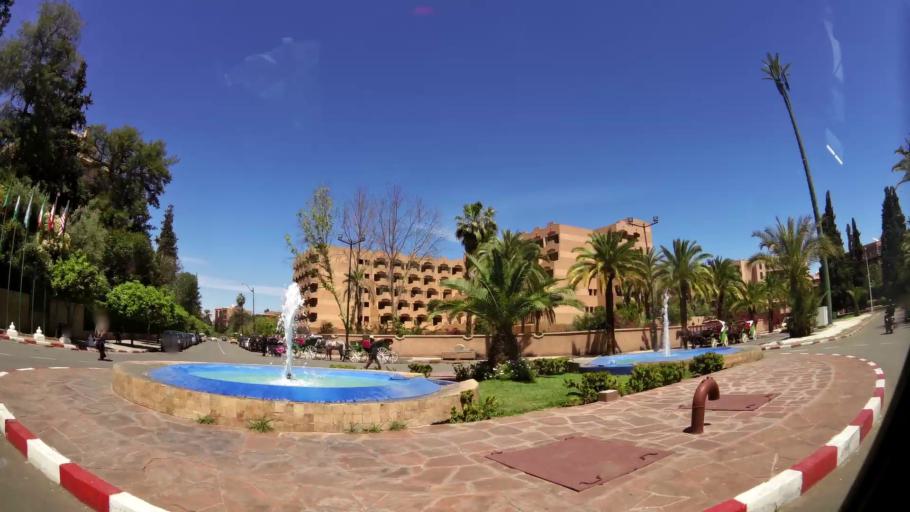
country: MA
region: Marrakech-Tensift-Al Haouz
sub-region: Marrakech
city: Marrakesh
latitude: 31.6218
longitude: -8.0035
